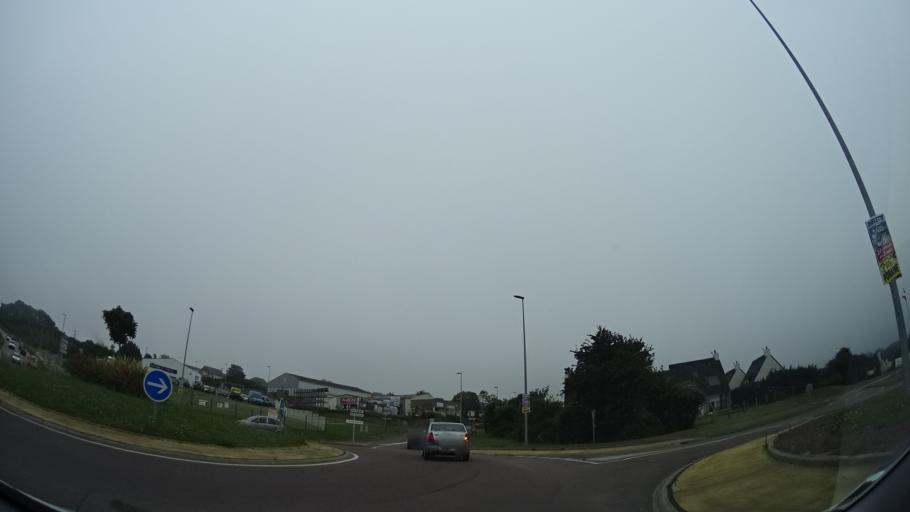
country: FR
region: Lower Normandy
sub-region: Departement de la Manche
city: Les Pieux
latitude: 49.5181
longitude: -1.8122
